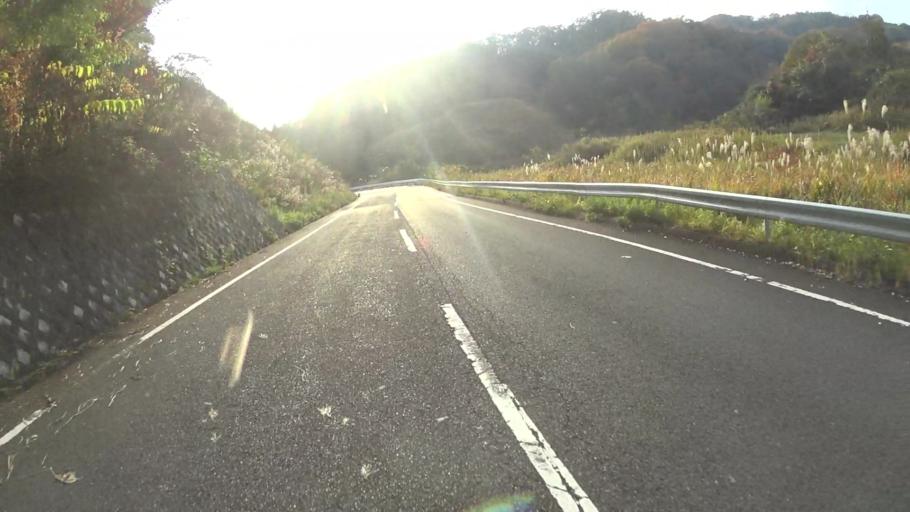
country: JP
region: Kyoto
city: Maizuru
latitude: 35.5149
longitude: 135.4585
